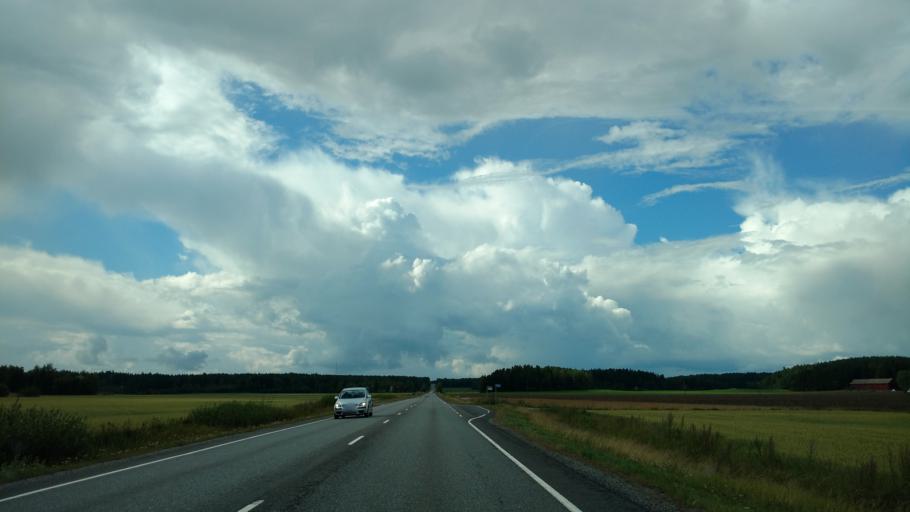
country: FI
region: Varsinais-Suomi
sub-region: Turku
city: Sauvo
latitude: 60.3920
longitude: 22.8655
